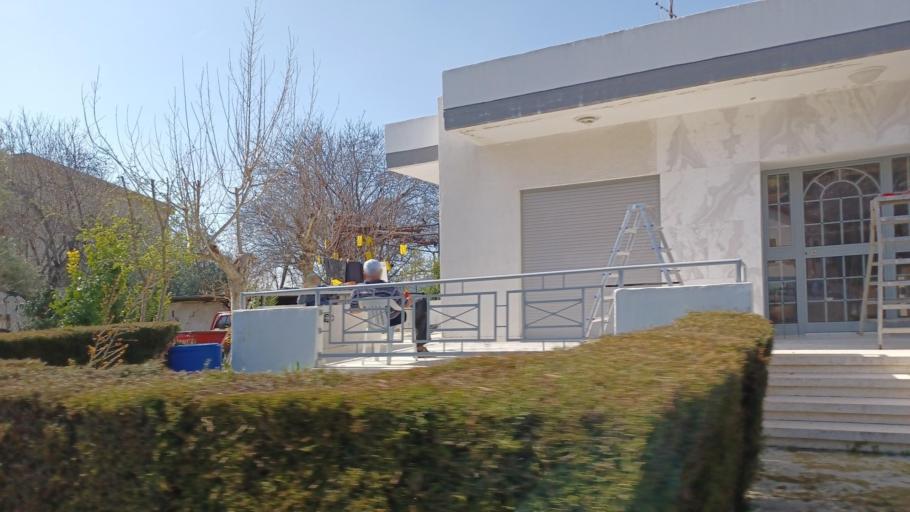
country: CY
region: Limassol
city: Pelendri
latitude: 34.8089
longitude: 32.9126
